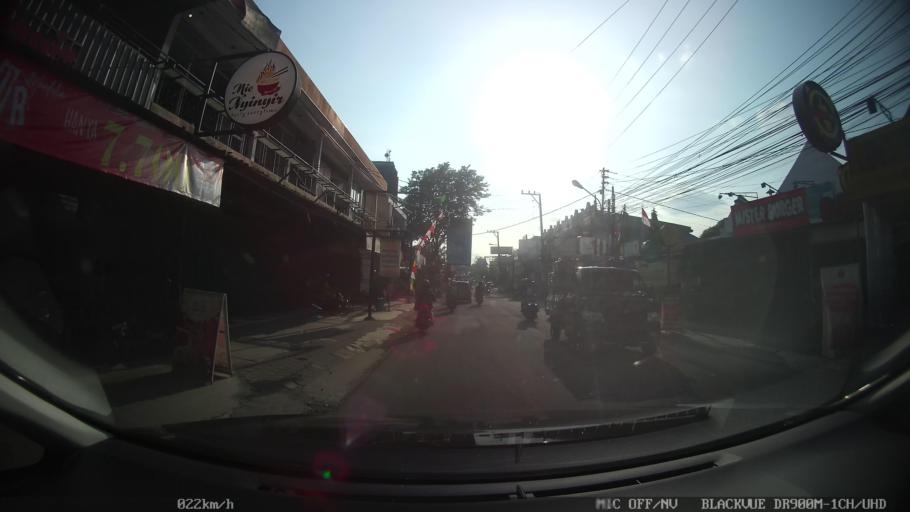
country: ID
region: Daerah Istimewa Yogyakarta
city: Depok
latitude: -7.7742
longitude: 110.4147
